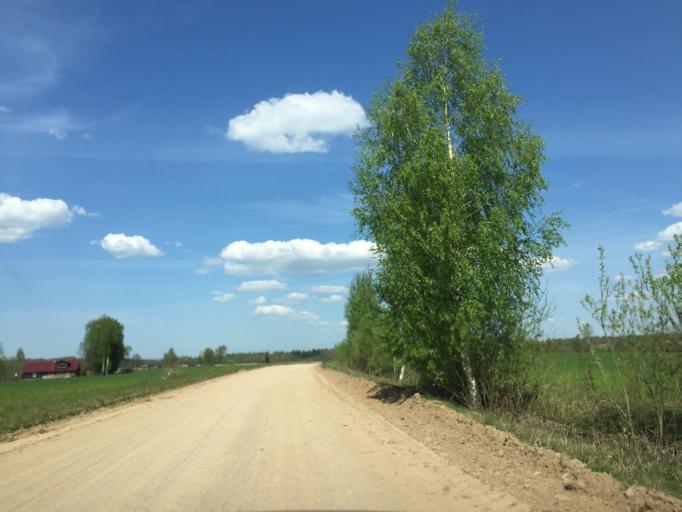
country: LV
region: Krimulda
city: Ragana
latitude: 57.3488
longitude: 24.6510
